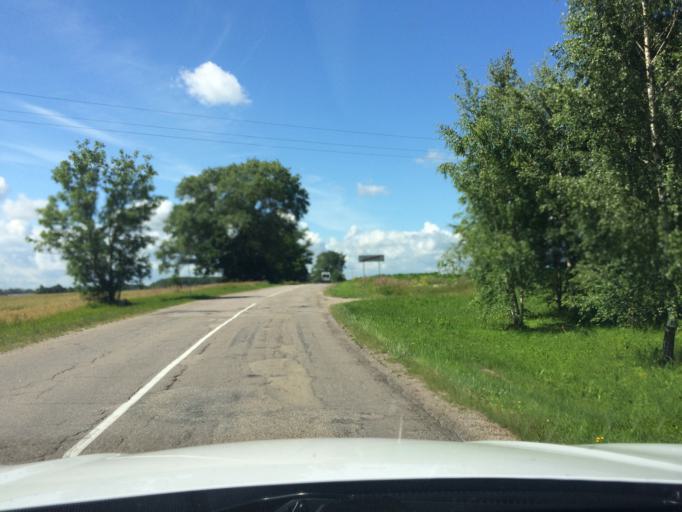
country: LV
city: Tervete
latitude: 56.5259
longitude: 23.5064
